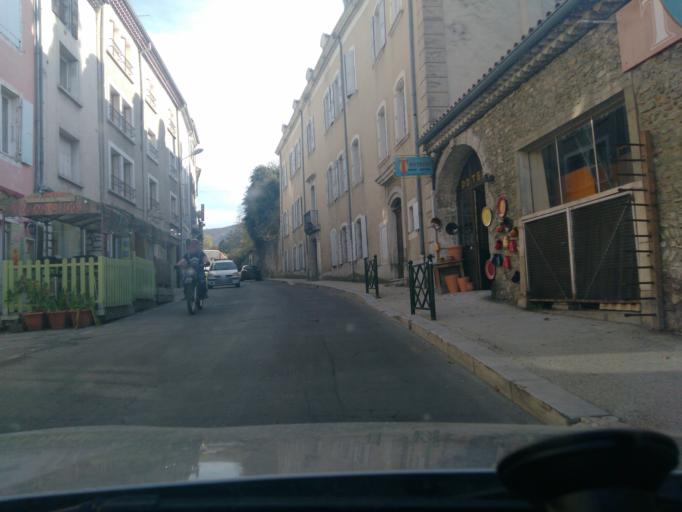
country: FR
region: Rhone-Alpes
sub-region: Departement de la Drome
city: Dieulefit
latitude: 44.5227
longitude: 5.0658
